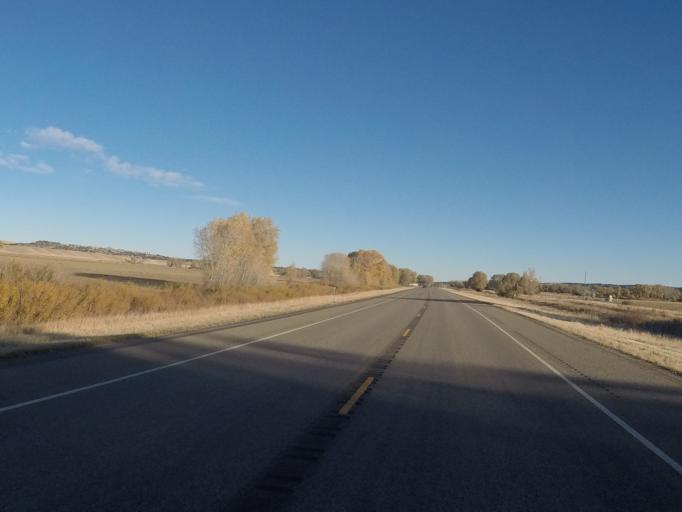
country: US
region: Montana
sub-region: Golden Valley County
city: Ryegate
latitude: 46.3486
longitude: -109.5366
